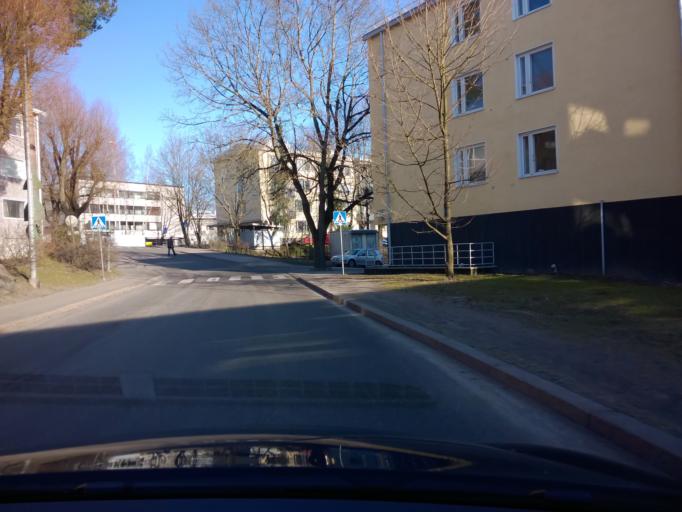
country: FI
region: Uusimaa
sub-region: Helsinki
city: Helsinki
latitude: 60.2160
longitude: 24.8958
